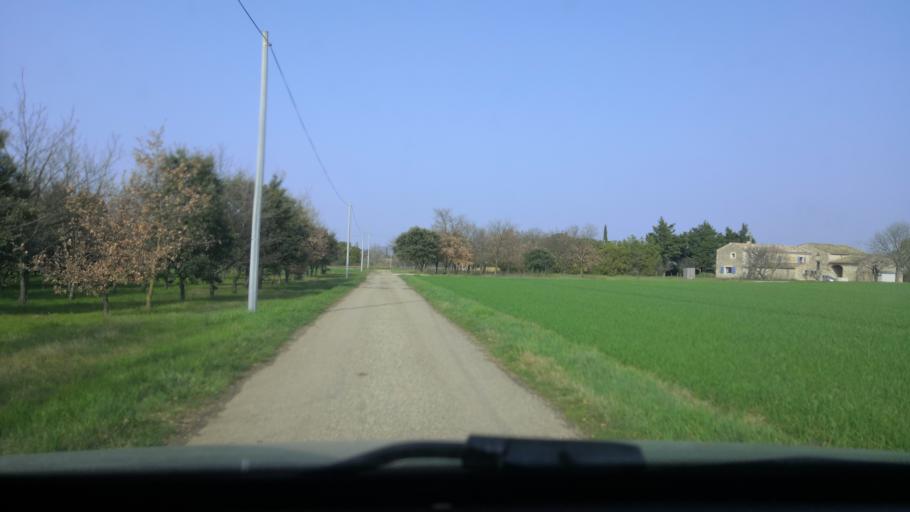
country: FR
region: Rhone-Alpes
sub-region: Departement de la Drome
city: La Begude-de-Mazenc
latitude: 44.5576
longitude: 4.8962
